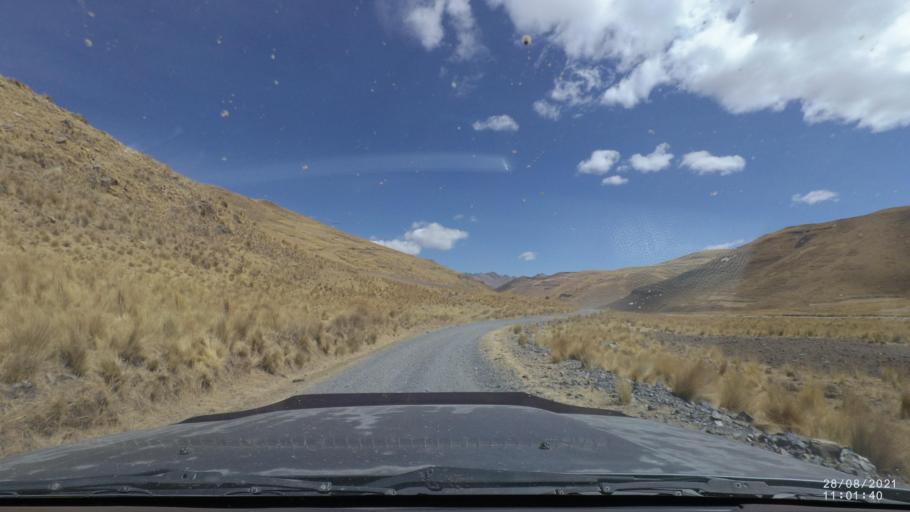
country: BO
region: Cochabamba
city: Cochabamba
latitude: -17.1802
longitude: -66.2683
